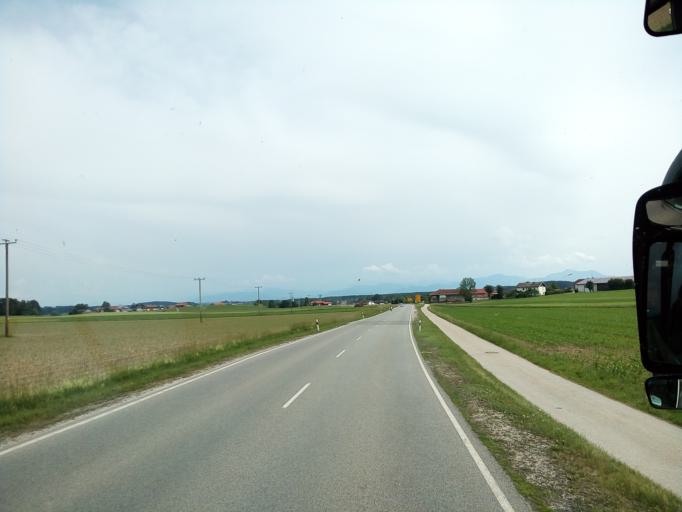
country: DE
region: Bavaria
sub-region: Upper Bavaria
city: Obing
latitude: 48.0195
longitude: 12.3806
